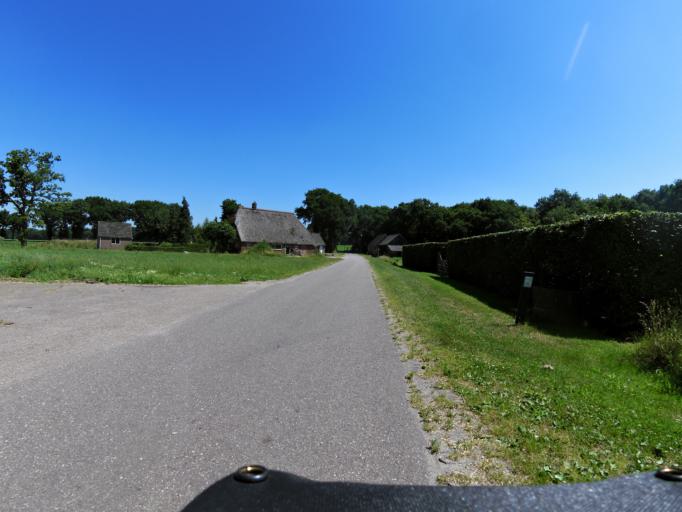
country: NL
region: Overijssel
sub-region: Gemeente Twenterand
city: Den Ham
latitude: 52.5022
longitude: 6.4302
